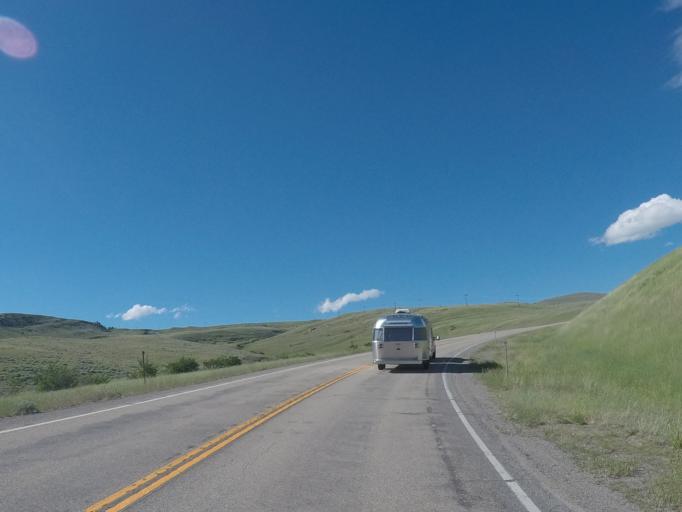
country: US
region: Montana
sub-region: Carbon County
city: Red Lodge
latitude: 45.1654
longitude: -109.2168
